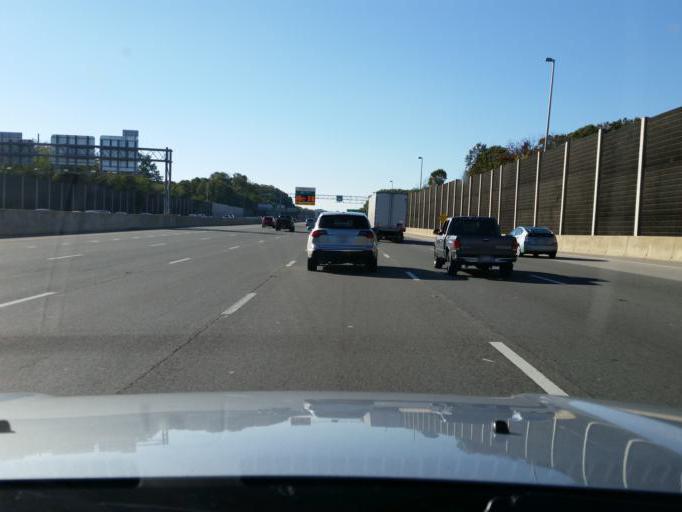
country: US
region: Virginia
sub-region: Fairfax County
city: Springfield
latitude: 38.7965
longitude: -77.1902
